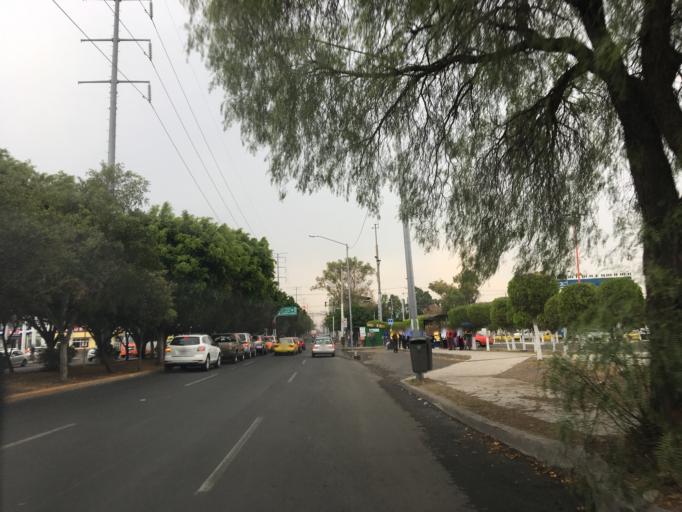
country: MX
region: Queretaro
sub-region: Queretaro
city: Santiago de Queretaro
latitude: 20.5778
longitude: -100.3733
